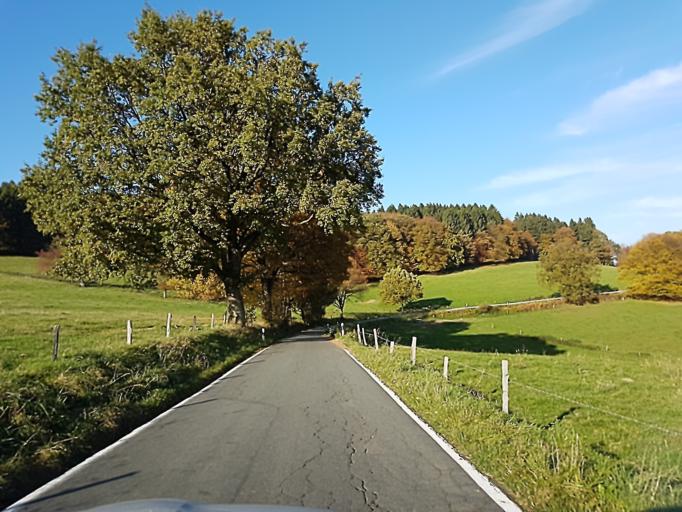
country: DE
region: North Rhine-Westphalia
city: Bergneustadt
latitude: 51.0604
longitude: 7.6159
